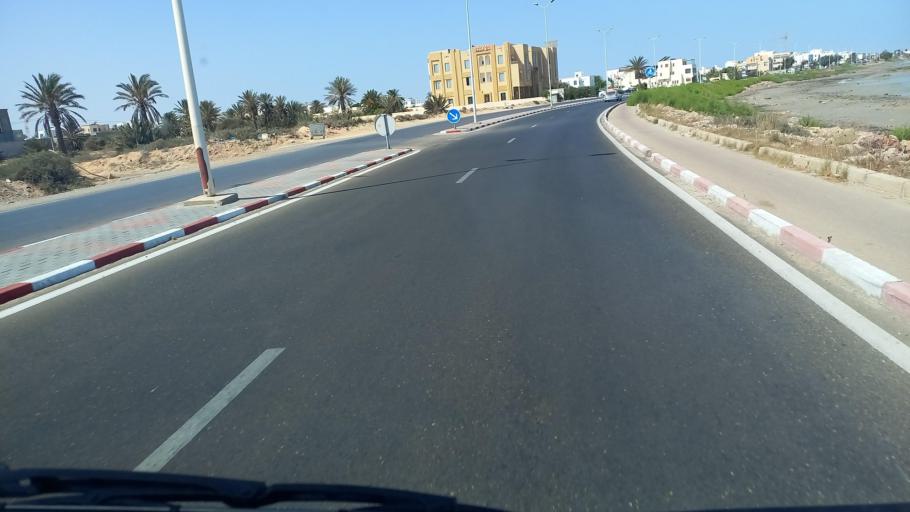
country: TN
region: Madanin
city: Houmt Souk
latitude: 33.8740
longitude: 10.8996
